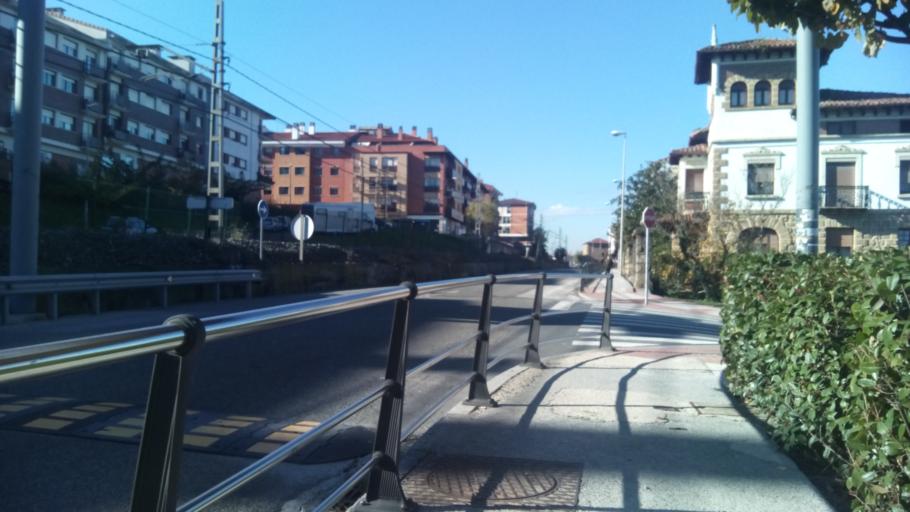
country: ES
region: Basque Country
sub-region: Bizkaia
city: Zamudio
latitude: 43.2831
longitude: -2.8606
